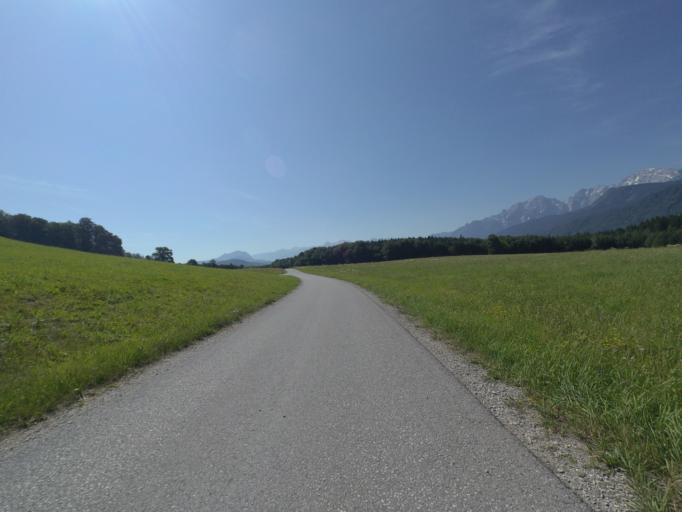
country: AT
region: Salzburg
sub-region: Politischer Bezirk Hallein
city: Adnet
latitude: 47.6851
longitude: 13.1264
